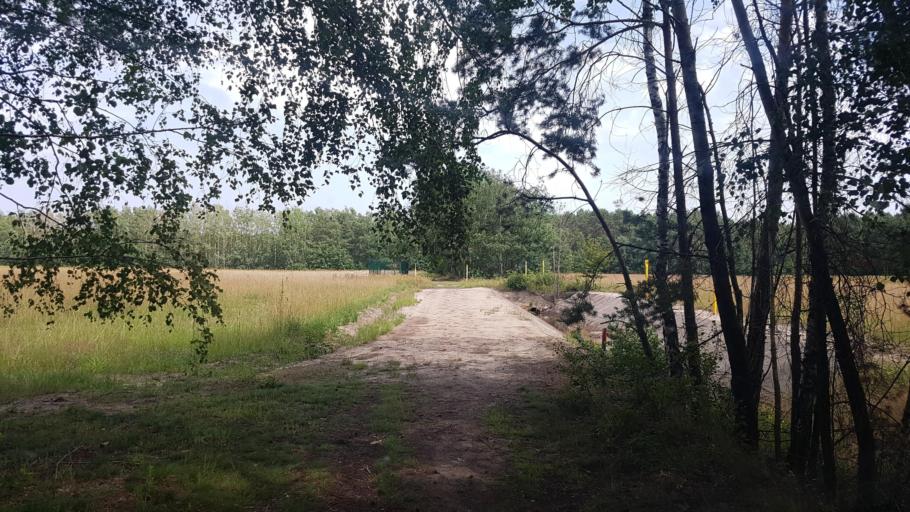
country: DE
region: Brandenburg
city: Finsterwalde
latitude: 51.6465
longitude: 13.6672
